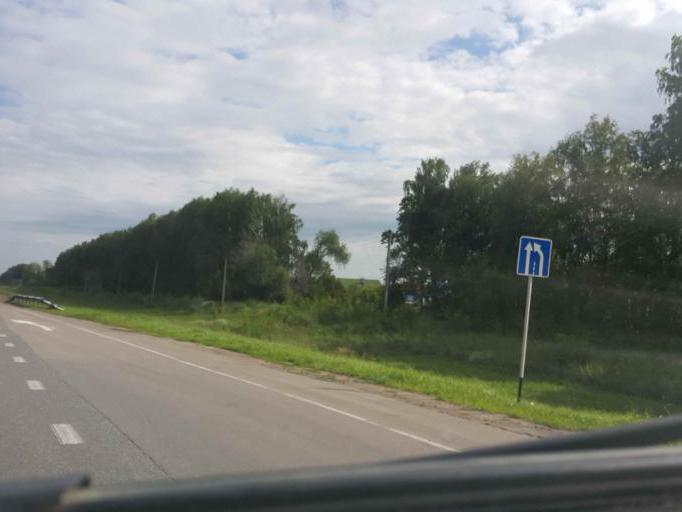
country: RU
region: Tambov
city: Bokino
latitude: 52.6178
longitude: 41.4438
